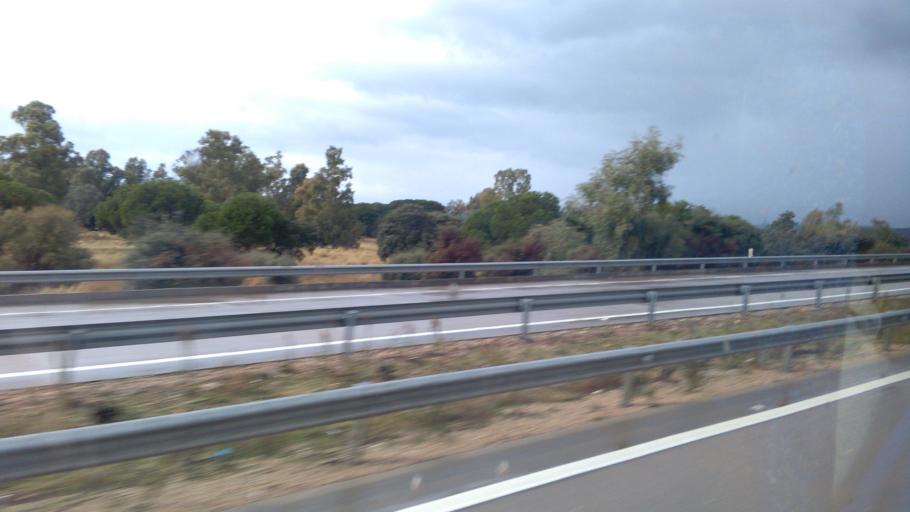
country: ES
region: Castille-La Mancha
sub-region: Province of Toledo
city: Cervera de los Montes
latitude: 39.9948
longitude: -4.7624
